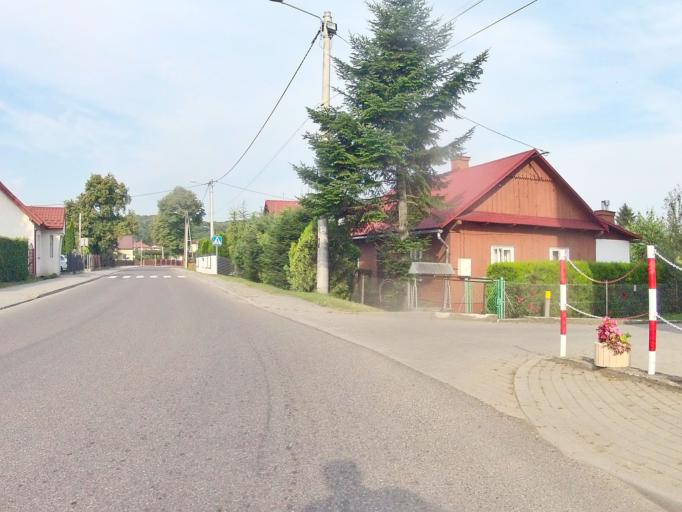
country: PL
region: Subcarpathian Voivodeship
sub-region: Powiat jasielski
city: Jaslo
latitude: 49.7178
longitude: 21.4613
